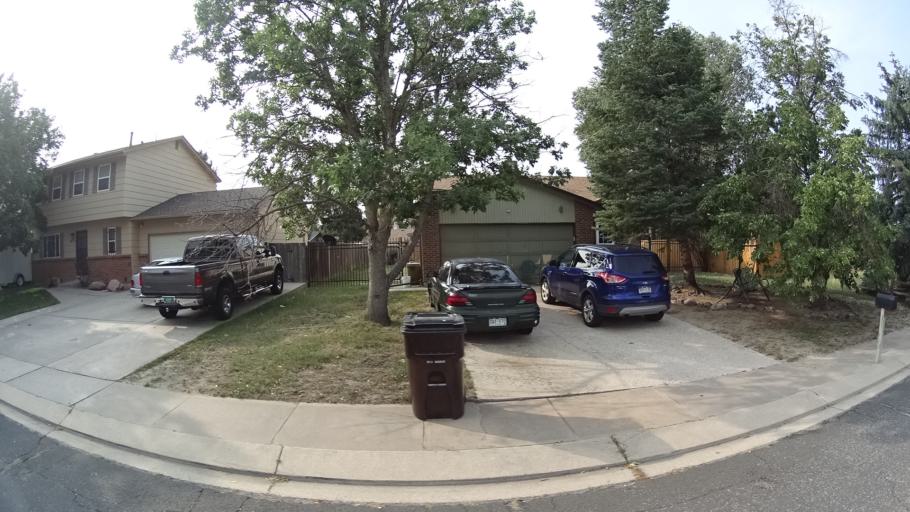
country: US
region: Colorado
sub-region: El Paso County
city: Stratmoor
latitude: 38.8003
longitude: -104.7427
